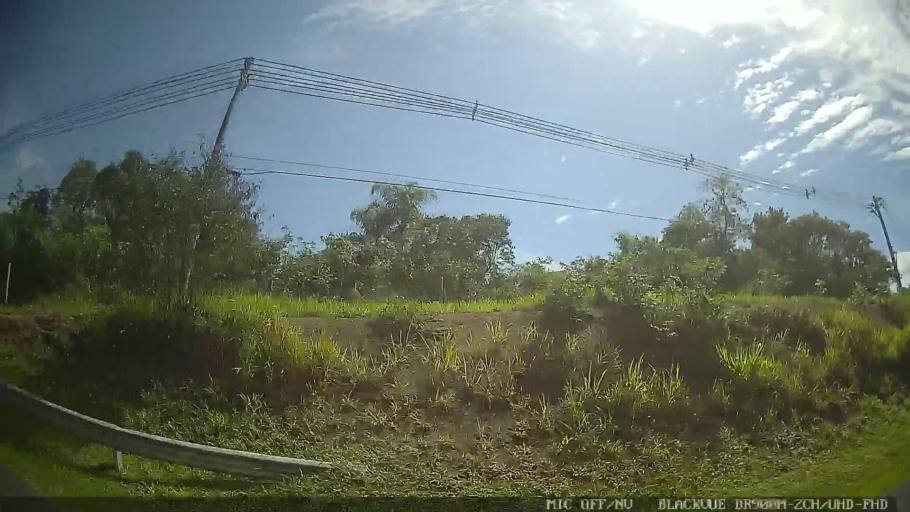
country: BR
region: Sao Paulo
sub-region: Porto Feliz
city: Porto Feliz
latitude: -23.2252
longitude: -47.5700
